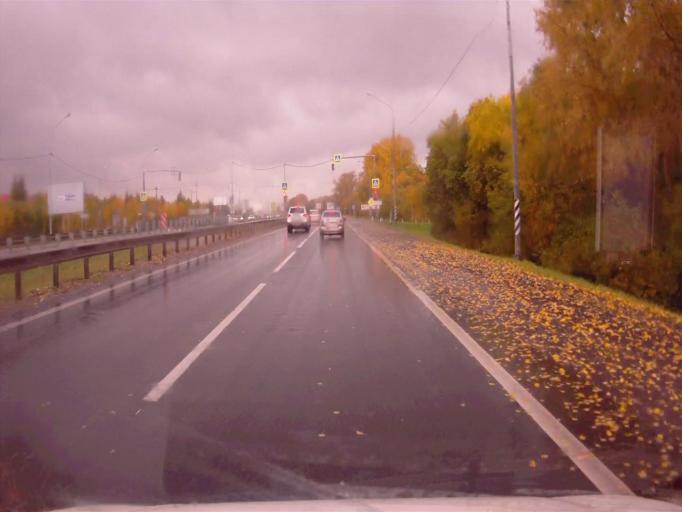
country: RU
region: Chelyabinsk
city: Dolgoderevenskoye
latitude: 55.2824
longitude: 61.3431
